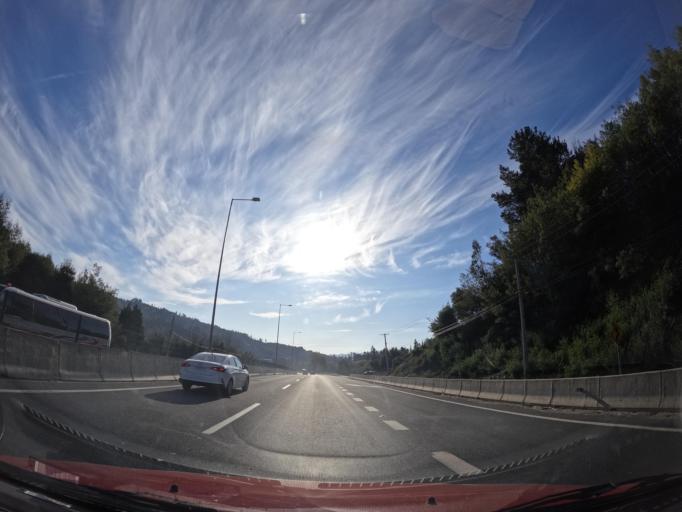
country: CL
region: Biobio
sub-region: Provincia de Concepcion
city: Penco
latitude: -36.8267
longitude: -72.9248
